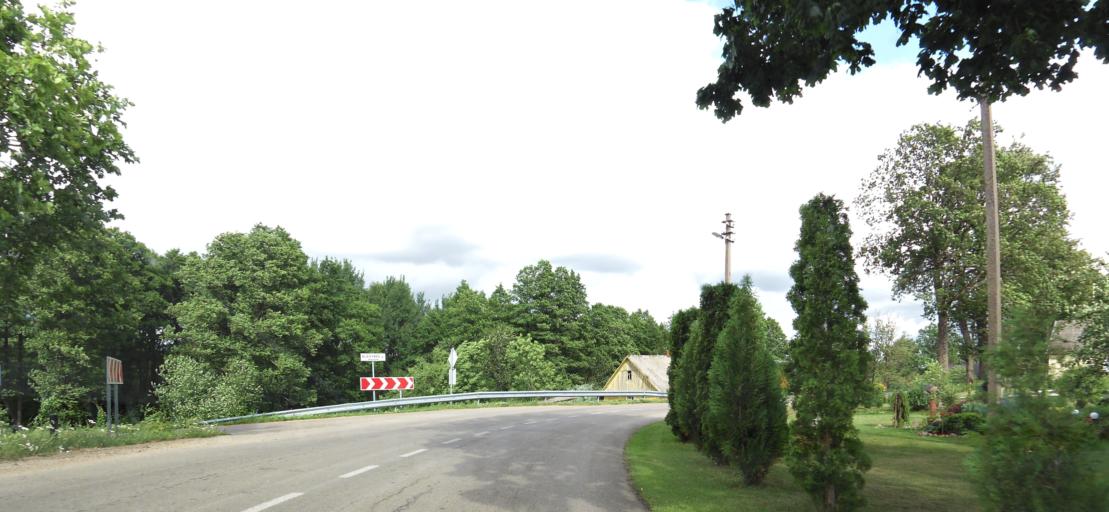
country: LT
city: Obeliai
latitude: 55.8910
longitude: 25.1950
